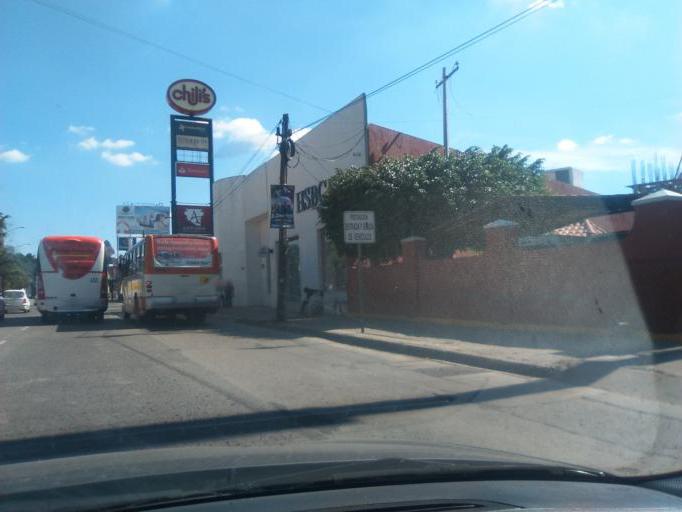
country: MX
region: Guanajuato
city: Leon
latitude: 21.1031
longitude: -101.6370
